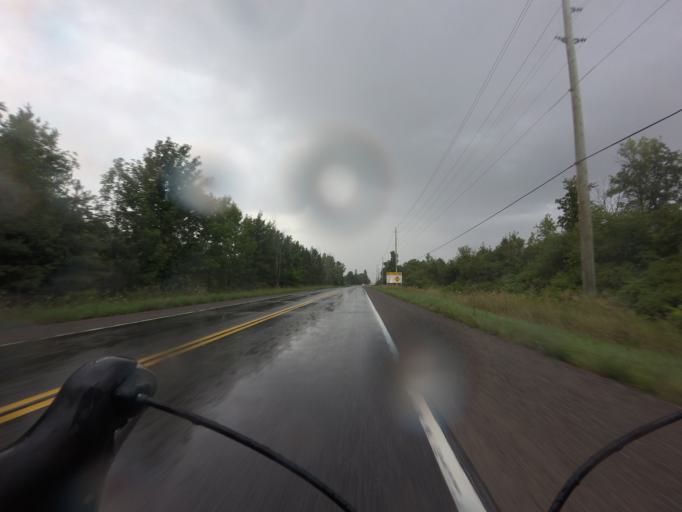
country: CA
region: Ontario
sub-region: Lanark County
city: Smiths Falls
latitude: 44.9497
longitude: -75.8227
